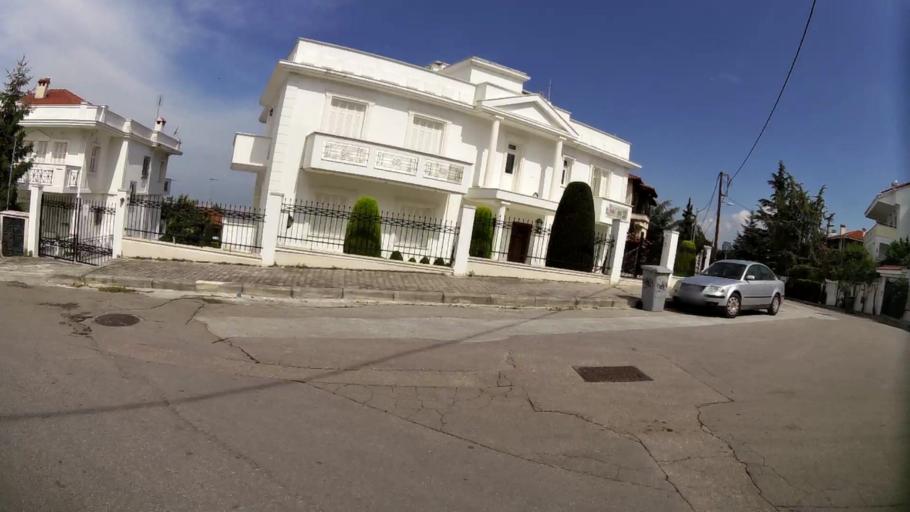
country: GR
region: Central Macedonia
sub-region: Nomos Thessalonikis
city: Panorama
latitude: 40.5794
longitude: 23.0217
